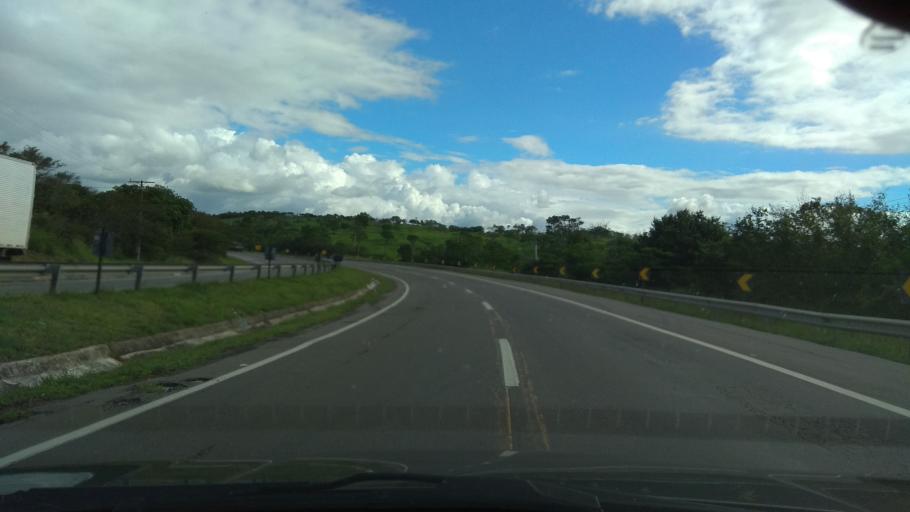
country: BR
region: Bahia
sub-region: Feira De Santana
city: Feira de Santana
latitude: -12.3430
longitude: -39.0868
